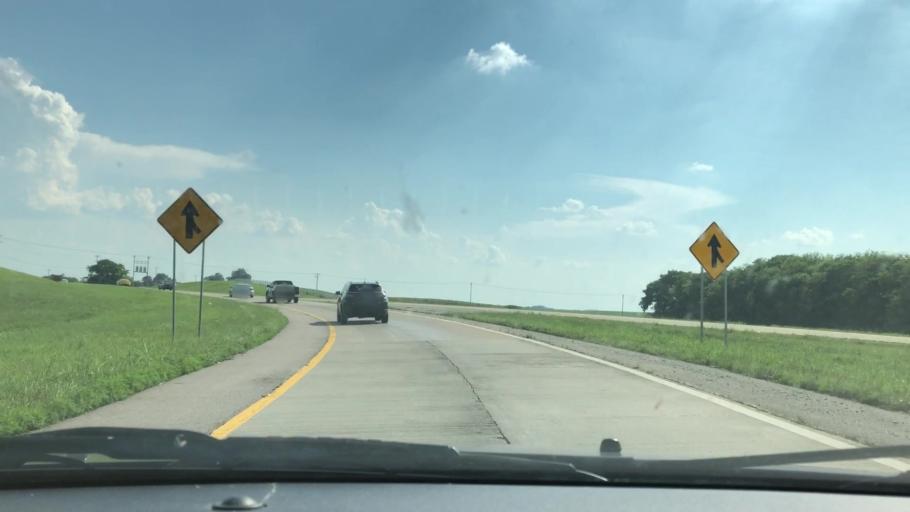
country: US
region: Tennessee
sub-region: Maury County
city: Spring Hill
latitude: 35.7397
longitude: -86.9491
